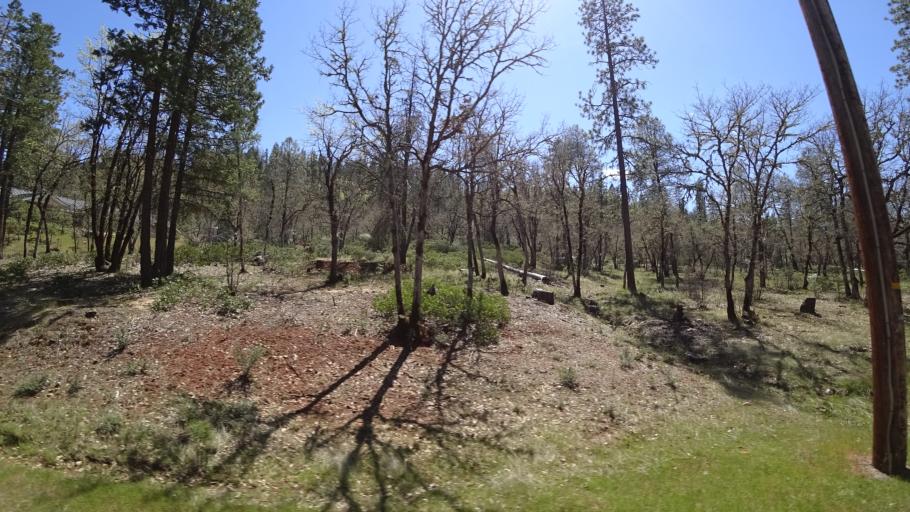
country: US
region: California
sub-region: Trinity County
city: Weaverville
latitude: 40.7528
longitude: -122.9043
